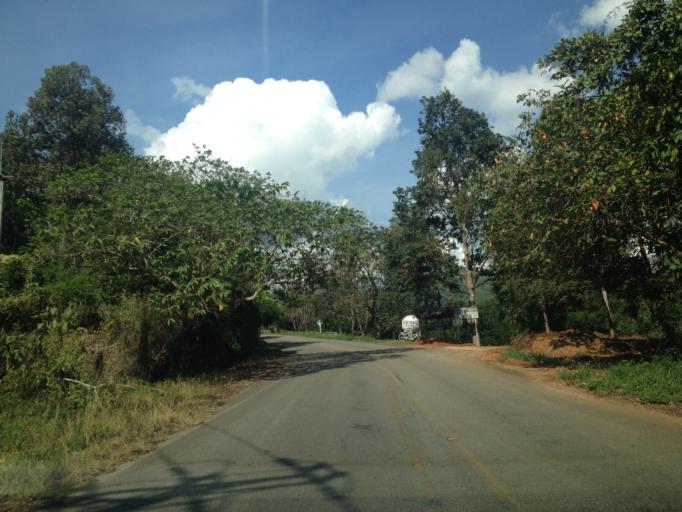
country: TH
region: Chiang Mai
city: Samoeng
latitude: 18.8100
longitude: 98.8174
